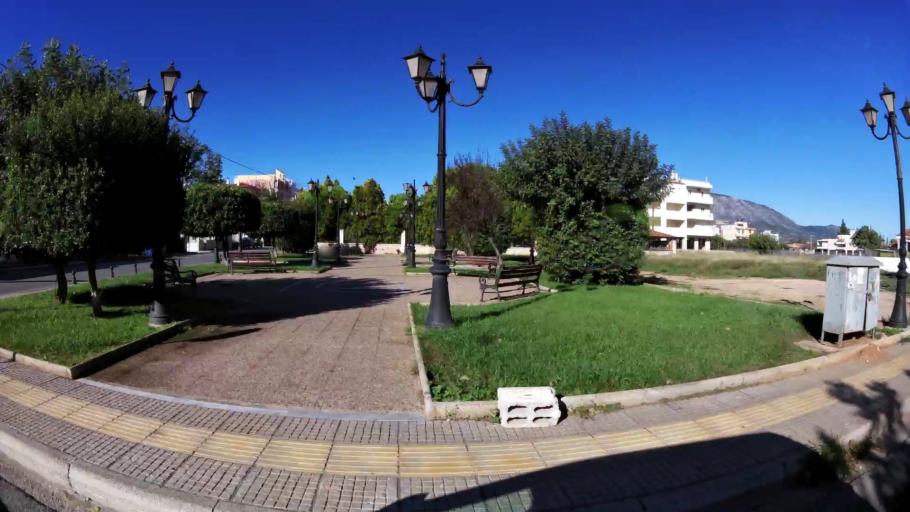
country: GR
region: Attica
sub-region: Nomarchia Anatolikis Attikis
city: Koropi
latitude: 37.9053
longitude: 23.8719
